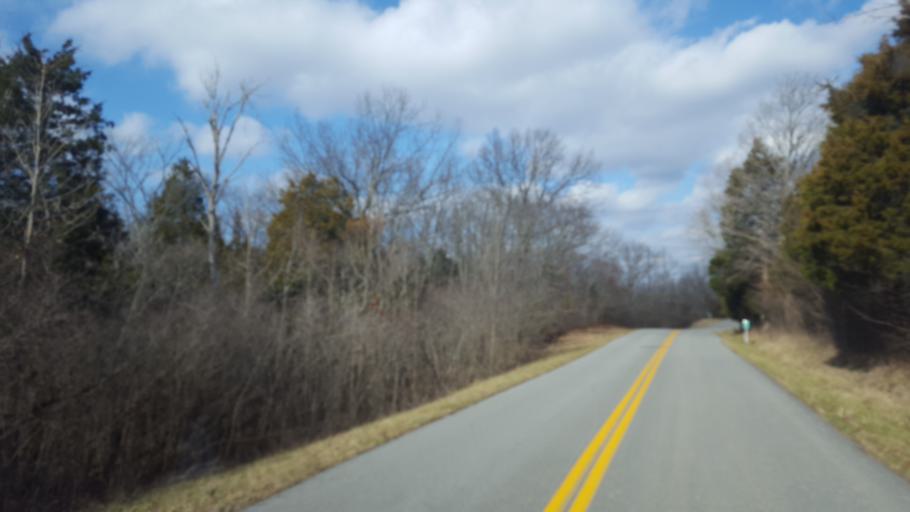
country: US
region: Kentucky
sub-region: Franklin County
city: Frankfort
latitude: 38.3768
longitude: -84.9479
